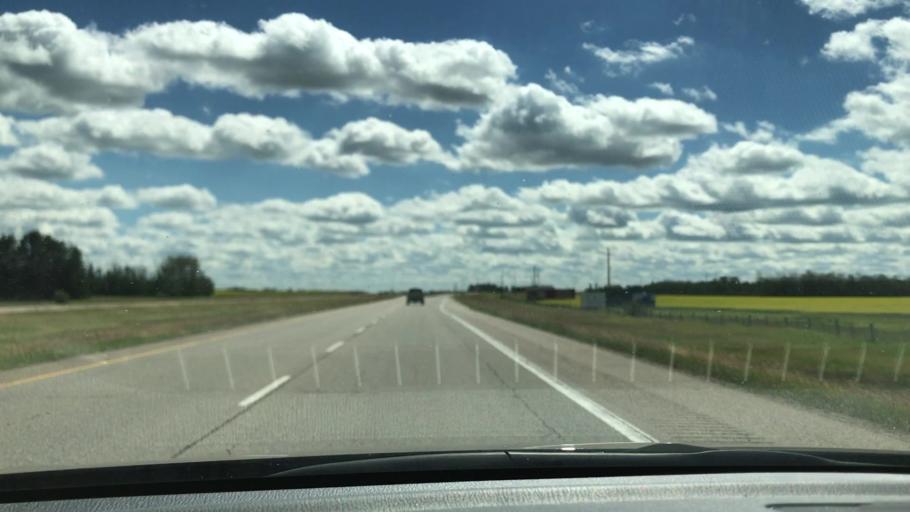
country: CA
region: Alberta
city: Leduc
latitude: 53.2383
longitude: -113.5659
